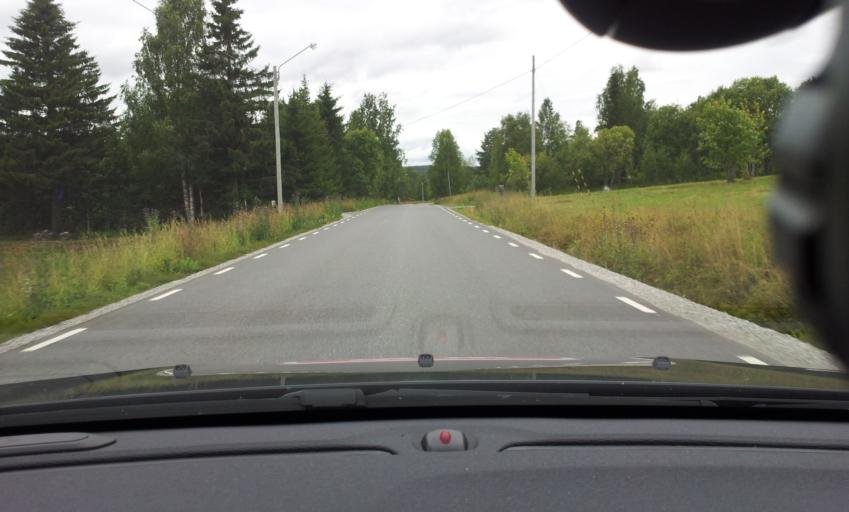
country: SE
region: Jaemtland
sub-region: Braecke Kommun
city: Braecke
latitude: 63.0792
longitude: 15.3982
